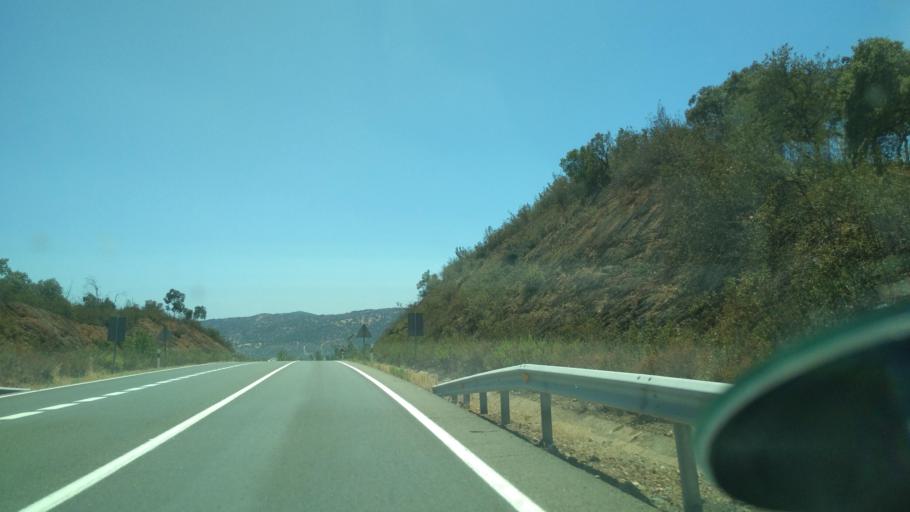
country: ES
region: Andalusia
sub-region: Provincia de Huelva
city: Campofrio
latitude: 37.8222
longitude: -6.5571
